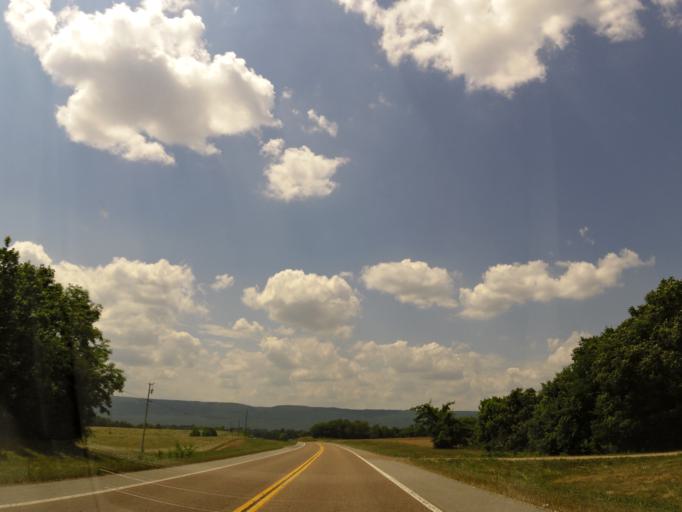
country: US
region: Tennessee
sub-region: Bledsoe County
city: Pikeville
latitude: 35.5837
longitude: -85.1716
